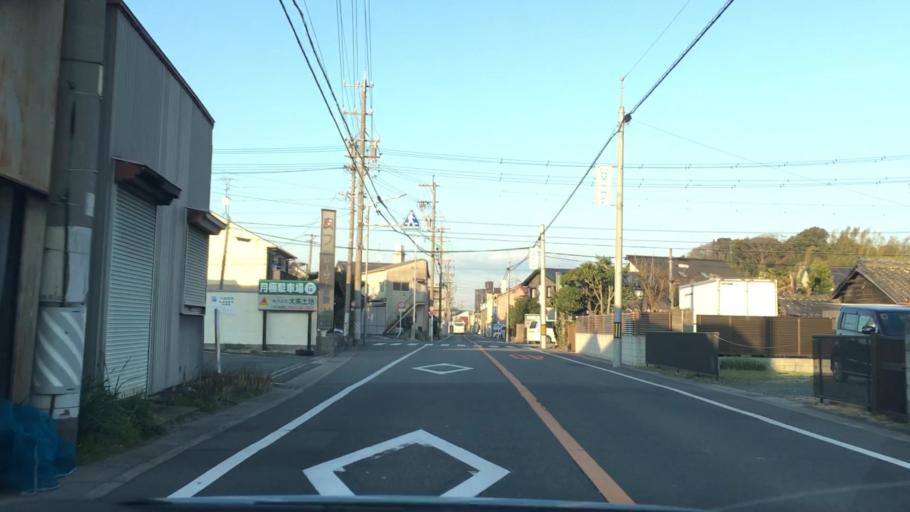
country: JP
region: Aichi
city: Obu
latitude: 35.0717
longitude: 136.9412
